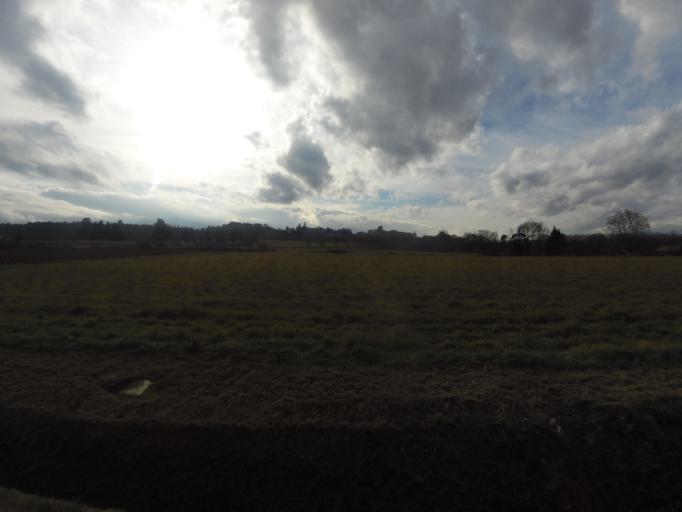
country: FR
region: Languedoc-Roussillon
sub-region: Departement du Gard
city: Saint-Mamert-du-Gard
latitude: 43.9001
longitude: 4.2201
